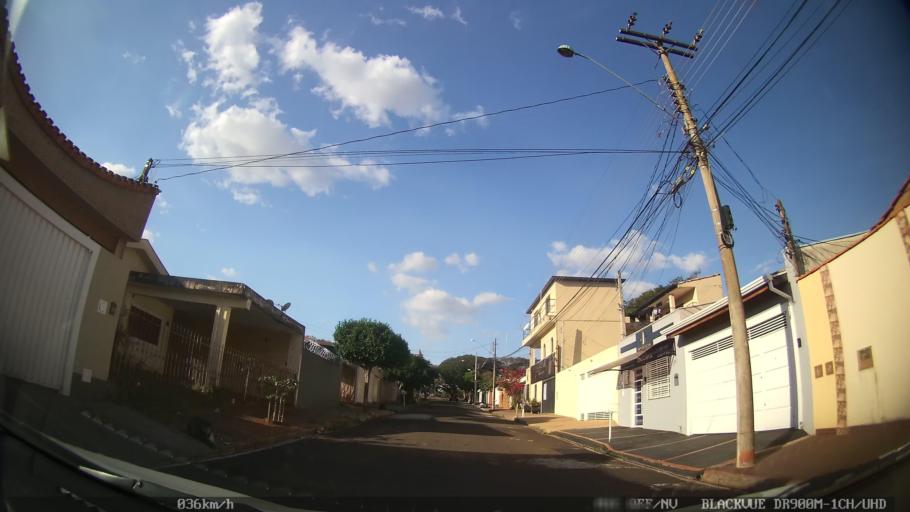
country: BR
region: Sao Paulo
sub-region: Ribeirao Preto
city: Ribeirao Preto
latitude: -21.1886
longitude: -47.7862
